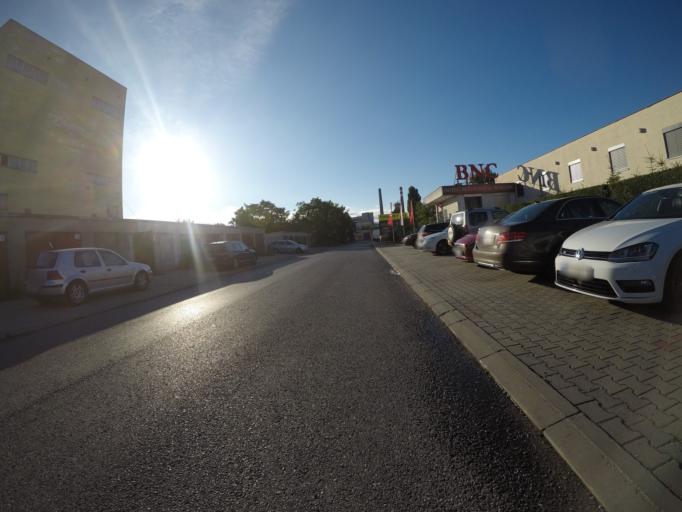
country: SK
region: Bratislavsky
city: Bratislava
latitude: 48.1723
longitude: 17.1569
